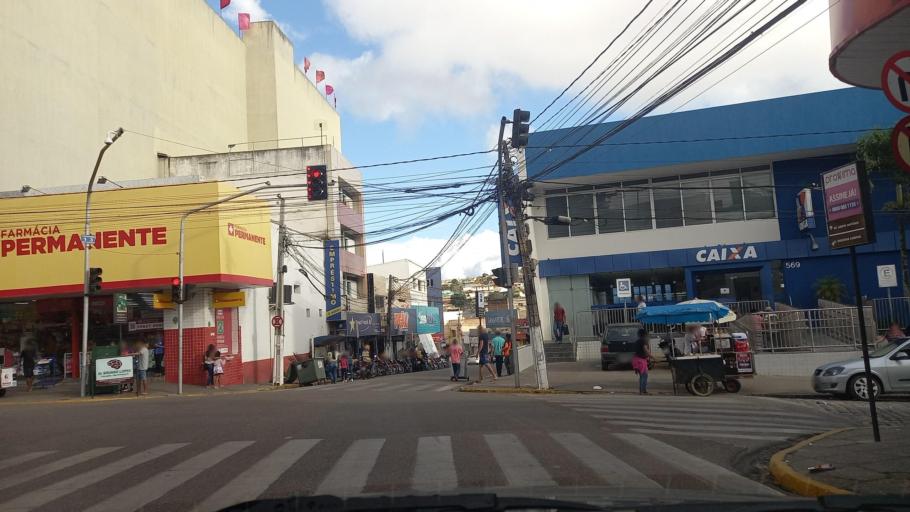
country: BR
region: Pernambuco
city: Garanhuns
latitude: -8.8912
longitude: -36.4965
